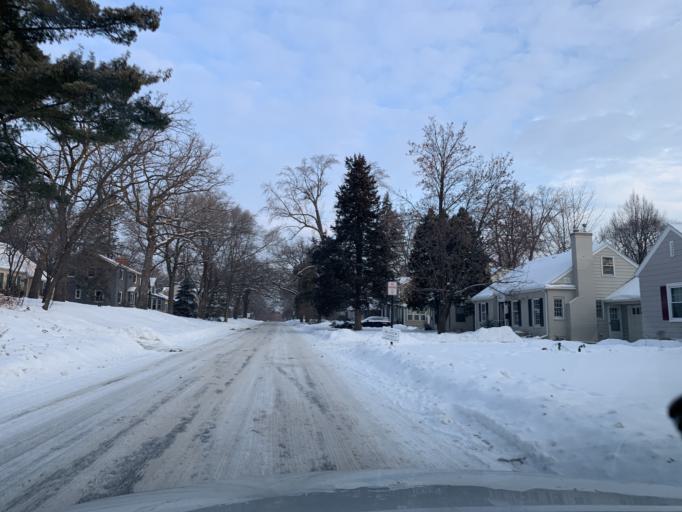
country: US
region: Minnesota
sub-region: Hennepin County
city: Saint Louis Park
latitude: 44.9247
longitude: -93.3580
